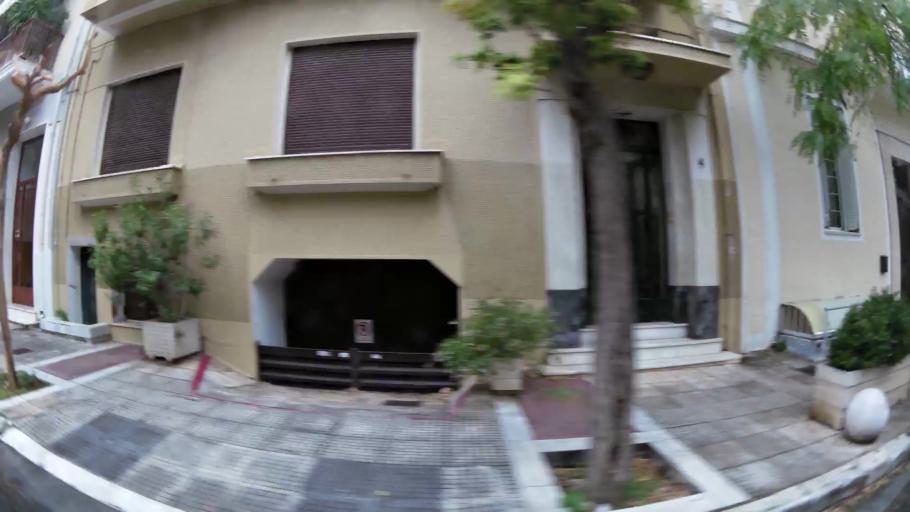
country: GR
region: Attica
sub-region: Nomarchia Athinas
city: Vyronas
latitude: 37.9669
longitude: 23.7421
